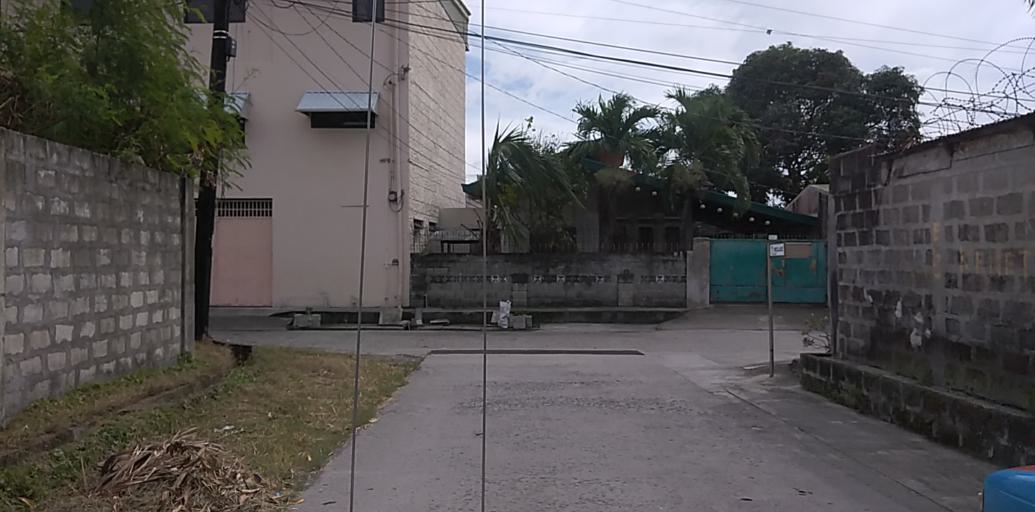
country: PH
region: Central Luzon
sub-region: Province of Pampanga
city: Manibaug Pasig
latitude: 15.1103
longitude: 120.5631
